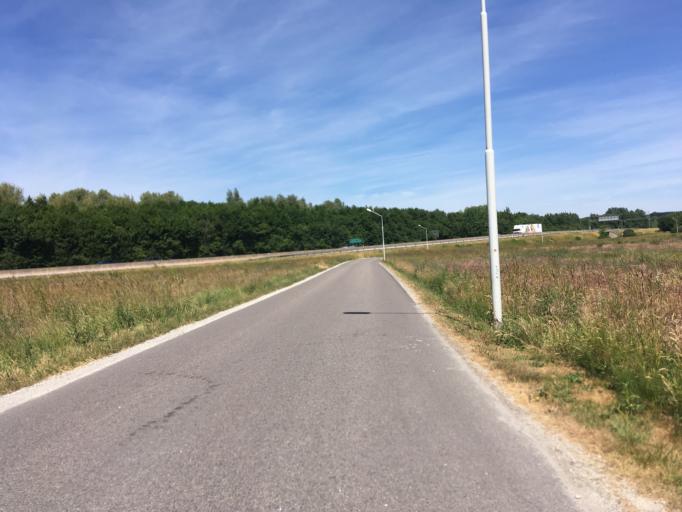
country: SE
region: Skane
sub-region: Lunds Kommun
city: Lund
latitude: 55.6897
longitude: 13.2064
